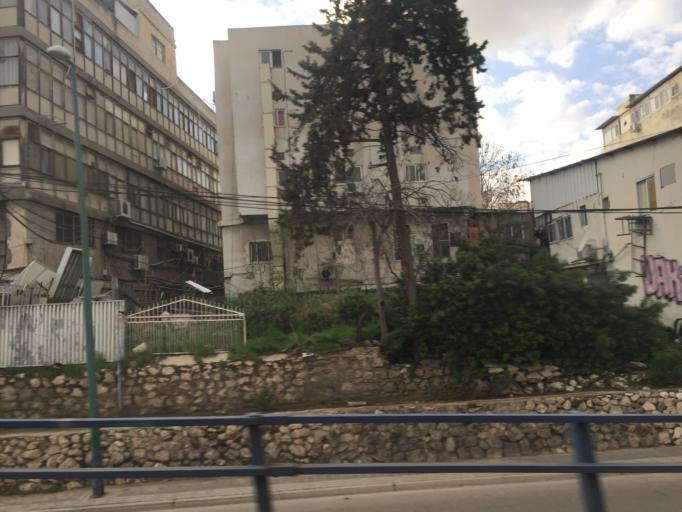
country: IL
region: Tel Aviv
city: Tel Aviv
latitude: 32.0573
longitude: 34.7837
